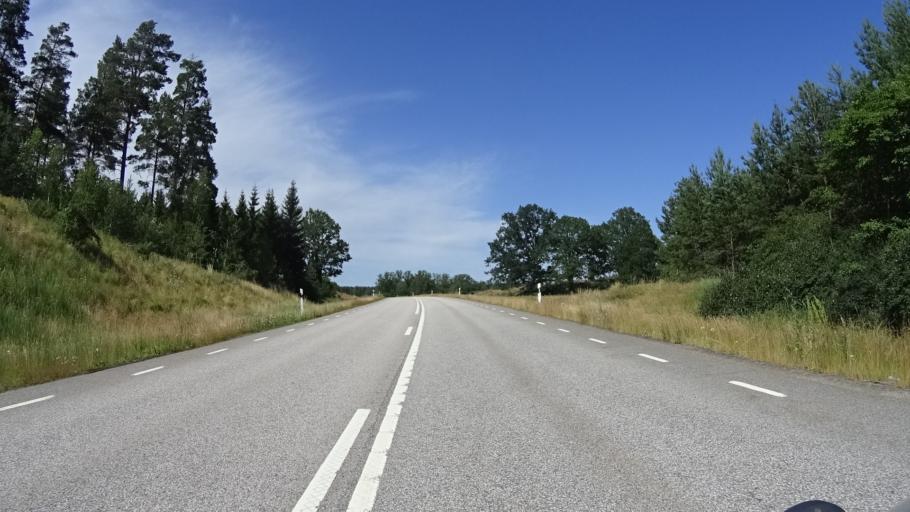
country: SE
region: Kalmar
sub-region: Vasterviks Kommun
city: Gamleby
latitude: 57.9395
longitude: 16.3846
